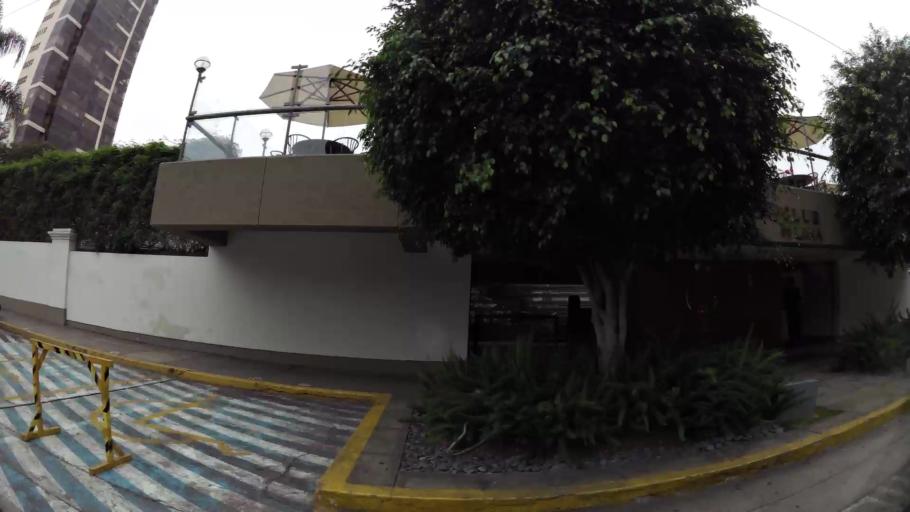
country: PE
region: Lima
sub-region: Lima
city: San Isidro
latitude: -12.0978
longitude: -77.0502
